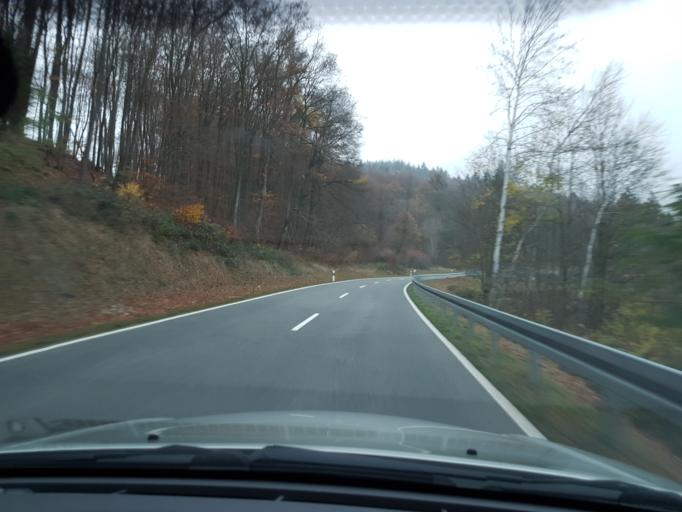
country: DE
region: Hesse
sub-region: Regierungsbezirk Darmstadt
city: Kiedrich
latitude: 50.0649
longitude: 8.0622
